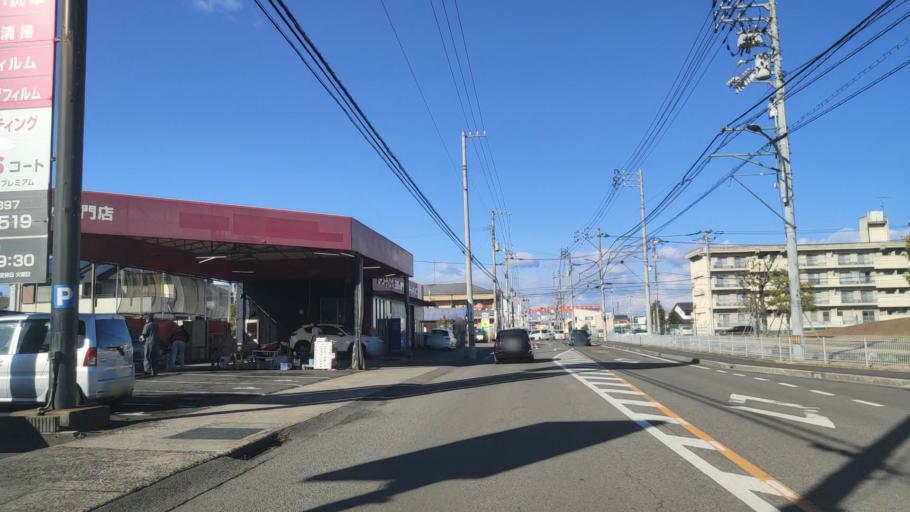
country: JP
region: Ehime
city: Saijo
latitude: 33.9176
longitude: 133.1919
